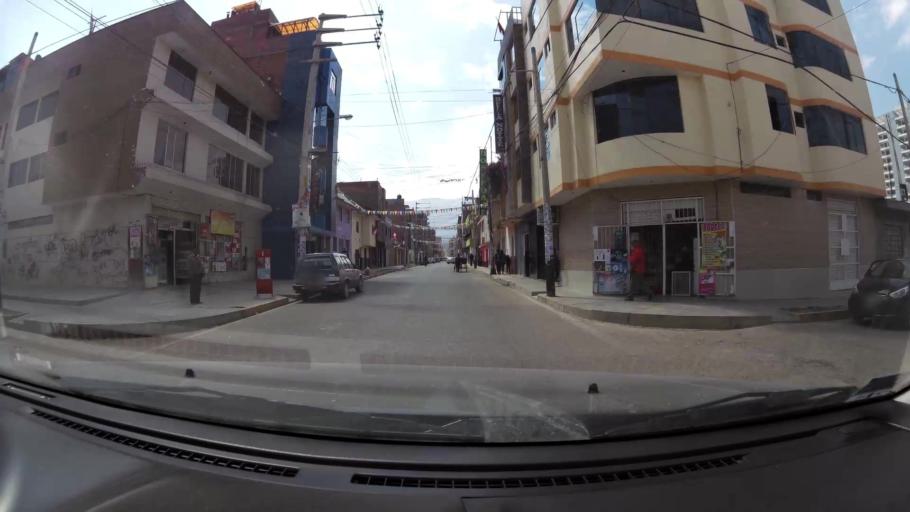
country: PE
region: Junin
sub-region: Provincia de Huancayo
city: El Tambo
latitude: -12.0726
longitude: -75.2156
